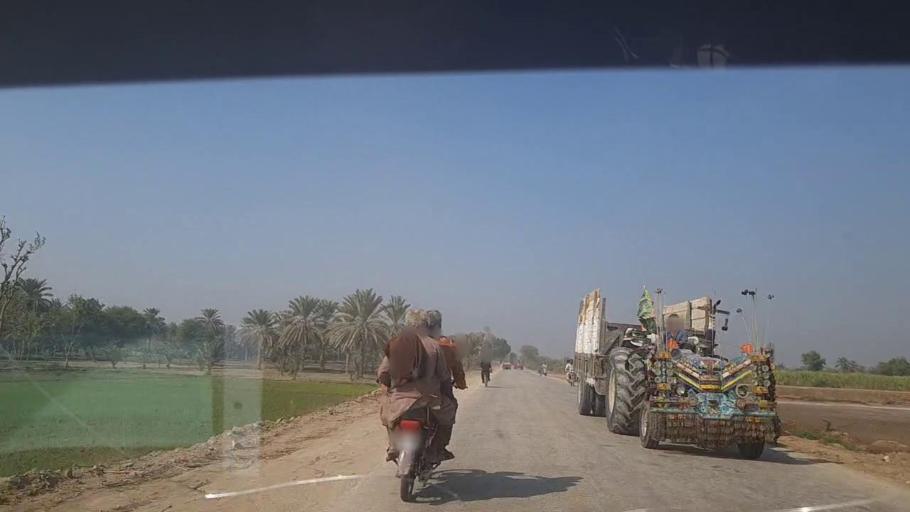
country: PK
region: Sindh
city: Kot Diji
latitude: 27.4167
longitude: 68.6637
